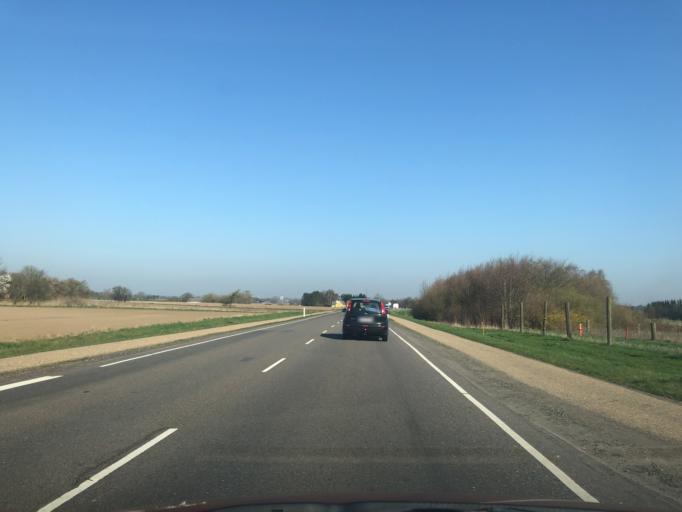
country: DK
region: Zealand
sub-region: Ringsted Kommune
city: Ringsted
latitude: 55.3952
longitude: 11.8396
